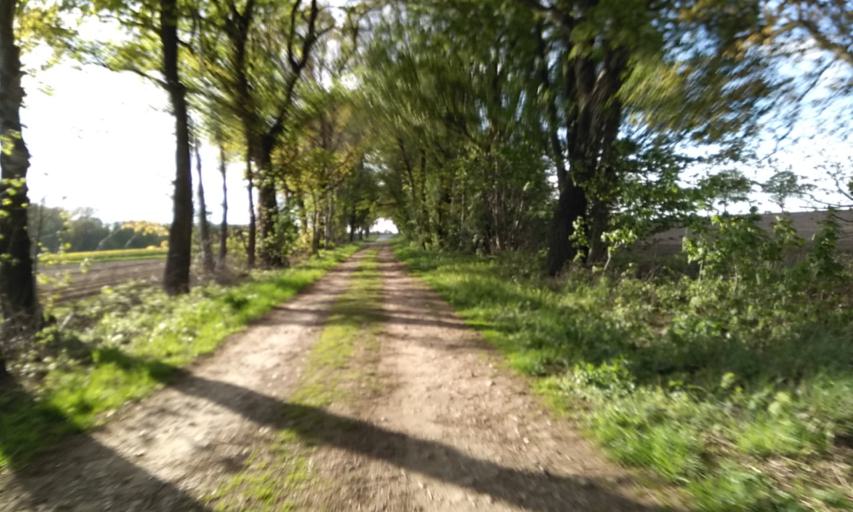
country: DE
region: Lower Saxony
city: Beckdorf
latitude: 53.4112
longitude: 9.6382
